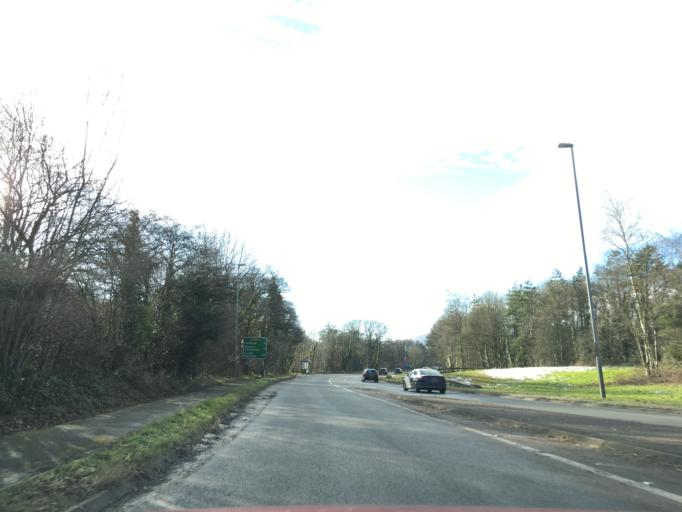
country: GB
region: Wales
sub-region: Torfaen County Borough
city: New Inn
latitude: 51.7191
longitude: -2.9897
